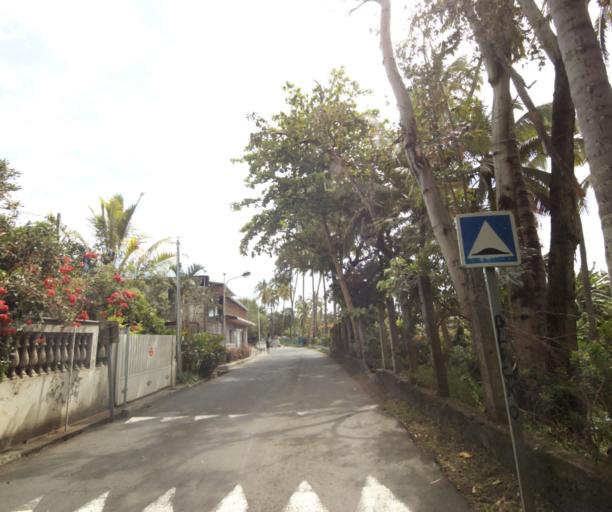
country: RE
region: Reunion
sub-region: Reunion
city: Saint-Paul
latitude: -21.0115
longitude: 55.2807
